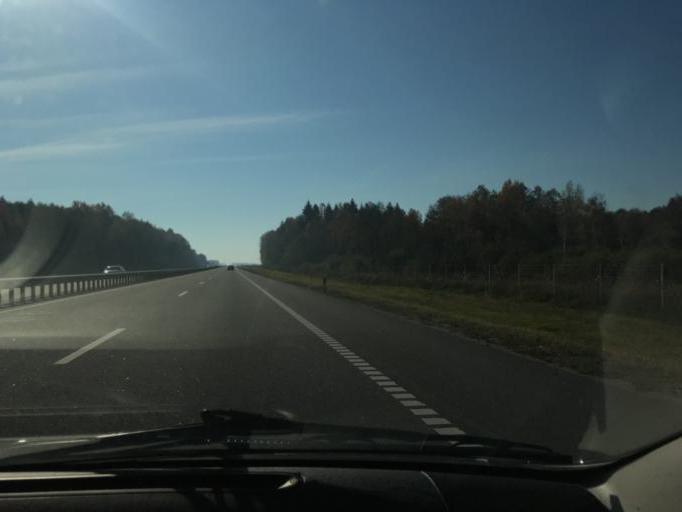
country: BY
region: Minsk
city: Slutsk
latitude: 53.2475
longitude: 27.5502
